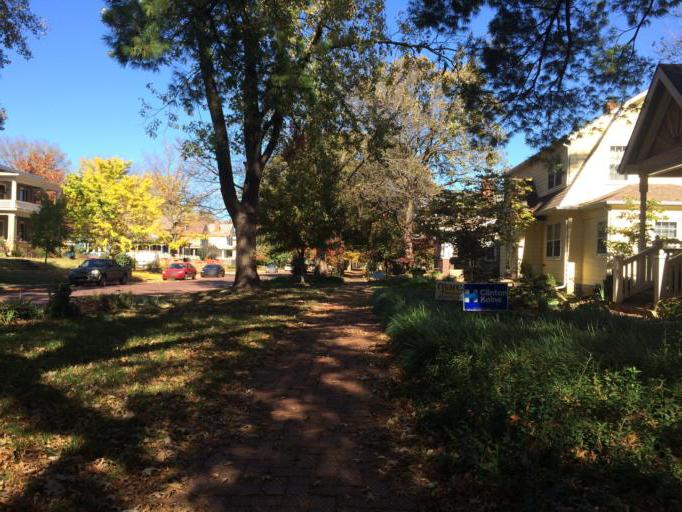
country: US
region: Kansas
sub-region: Douglas County
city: Lawrence
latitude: 38.9706
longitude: -95.2405
